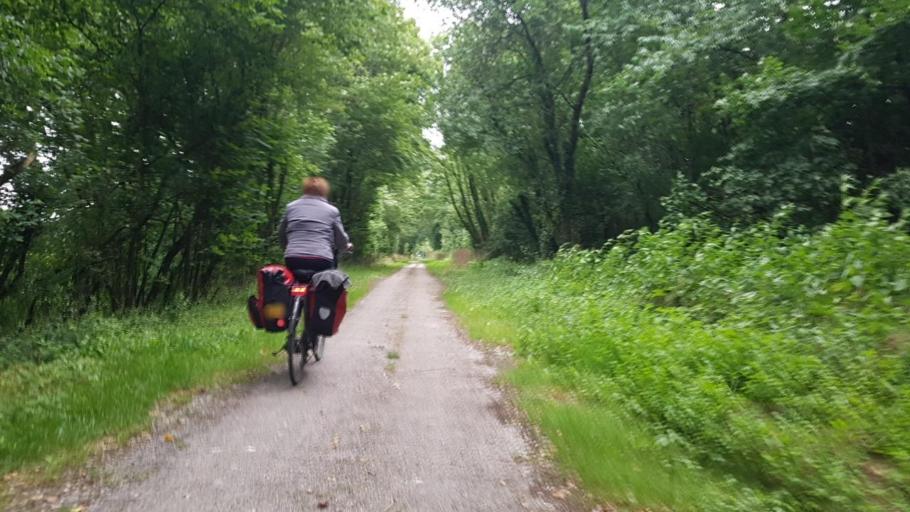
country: FR
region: Picardie
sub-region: Departement de l'Aisne
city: Buironfosse
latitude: 49.9062
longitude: 3.8529
